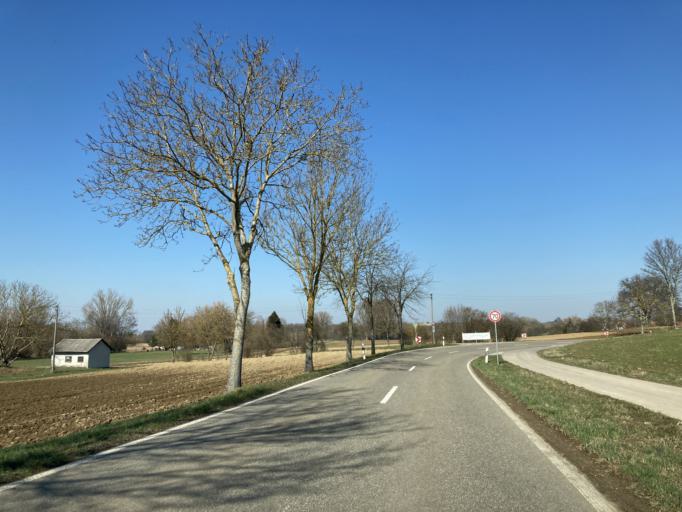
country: DE
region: Baden-Wuerttemberg
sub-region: Freiburg Region
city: Buggingen
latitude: 47.8304
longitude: 7.6518
